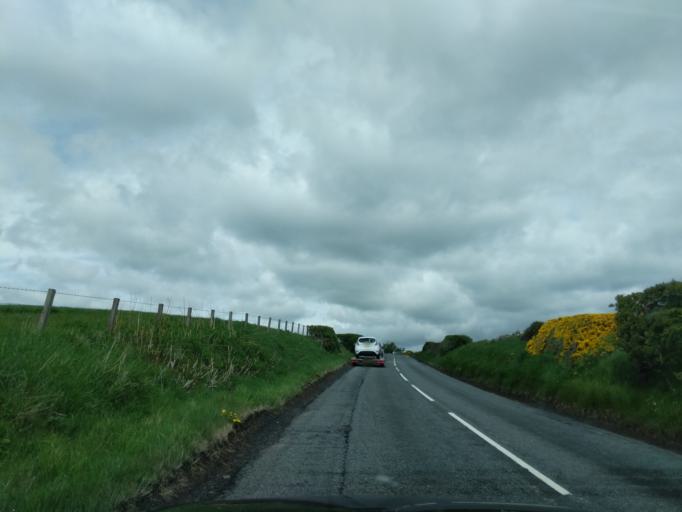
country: GB
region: Scotland
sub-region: The Scottish Borders
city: Earlston
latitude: 55.7002
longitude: -2.5998
